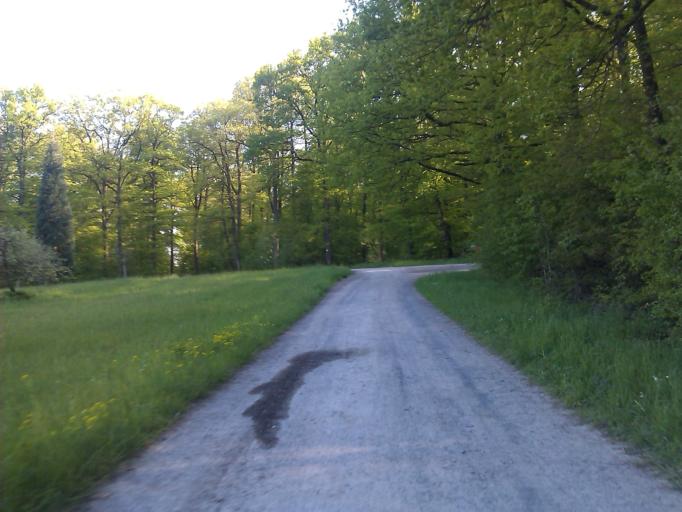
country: DE
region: Baden-Wuerttemberg
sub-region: Karlsruhe Region
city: Sternenfels
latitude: 49.0391
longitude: 8.8389
